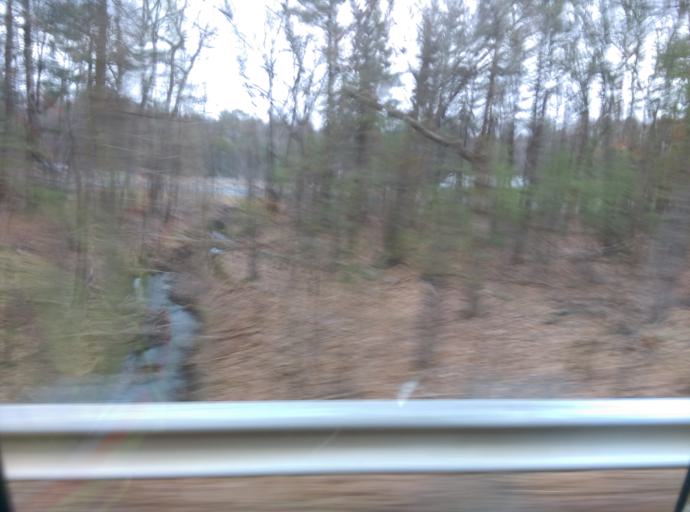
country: US
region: New Hampshire
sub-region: Rockingham County
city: Seabrook
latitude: 42.8755
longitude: -70.8873
